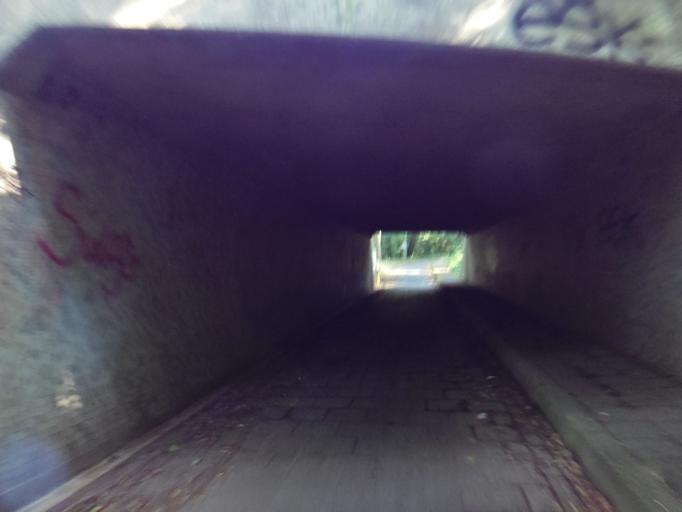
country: NL
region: Limburg
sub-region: Gemeente Kerkrade
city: Kerkrade
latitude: 50.8682
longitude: 6.0564
